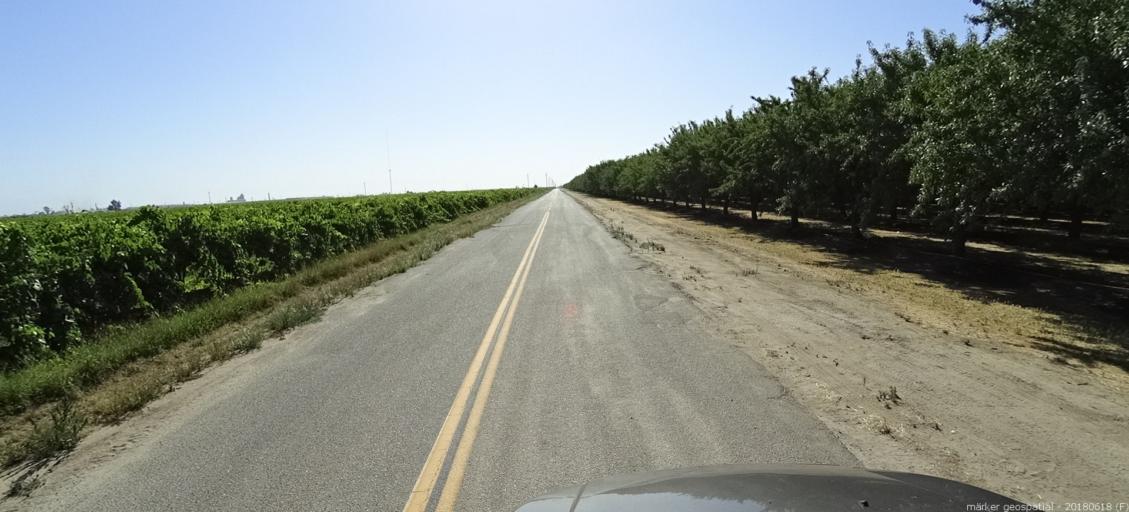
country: US
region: California
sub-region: Madera County
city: Madera
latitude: 36.9165
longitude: -120.1284
